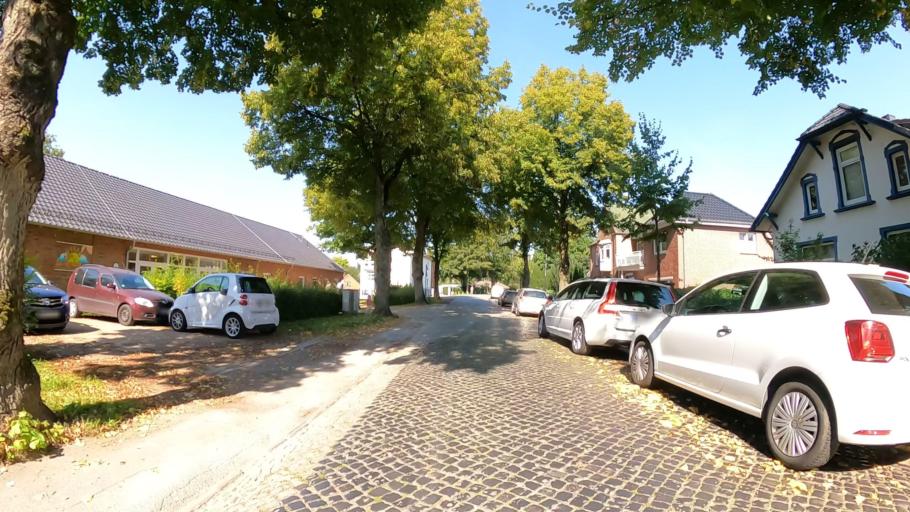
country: DE
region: Schleswig-Holstein
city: Bad Bramstedt
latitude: 53.9140
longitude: 9.8809
